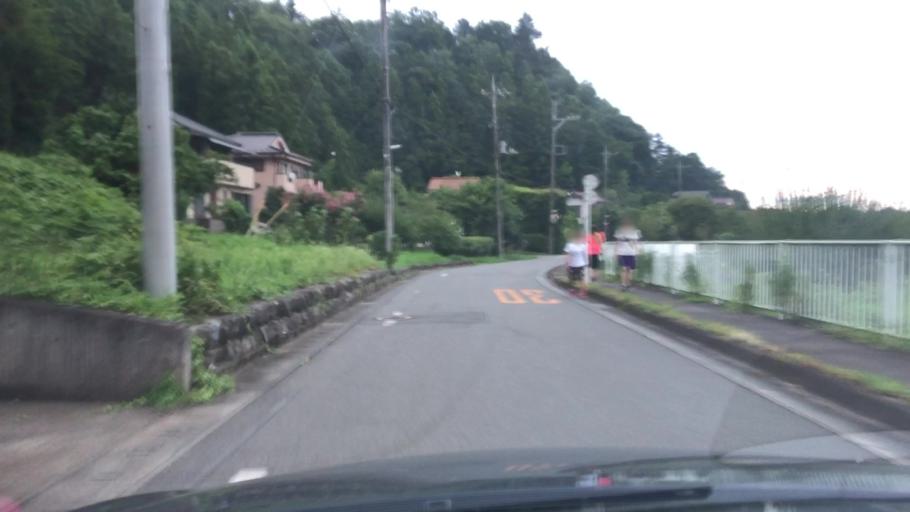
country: JP
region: Tokyo
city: Itsukaichi
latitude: 35.7459
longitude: 139.2464
